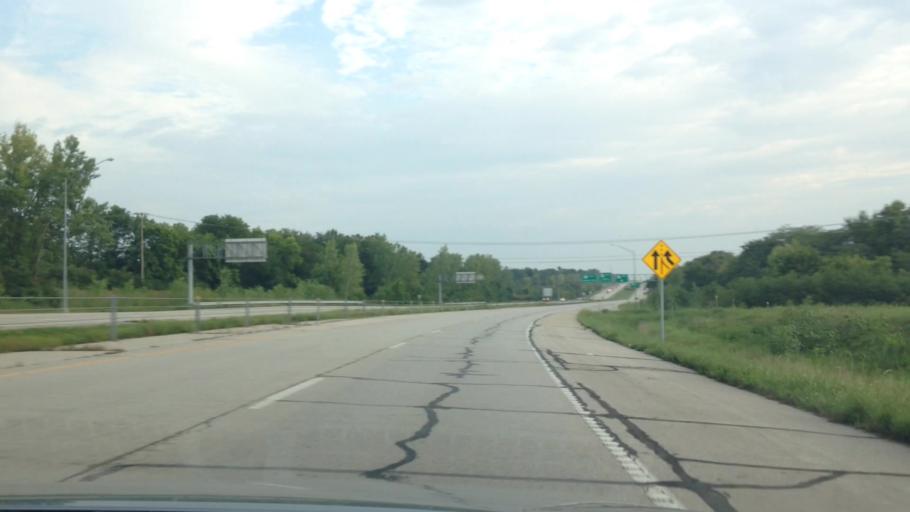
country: US
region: Missouri
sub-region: Clay County
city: Gladstone
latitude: 39.2680
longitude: -94.5850
